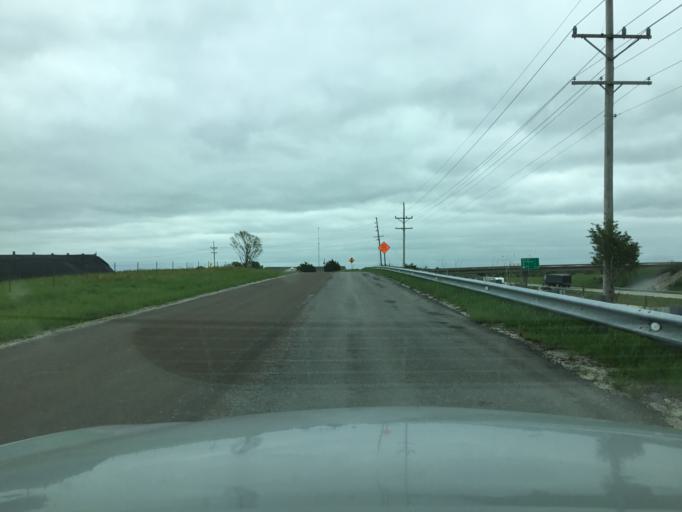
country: US
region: Kansas
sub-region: Franklin County
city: Ottawa
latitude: 38.5816
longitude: -95.2517
